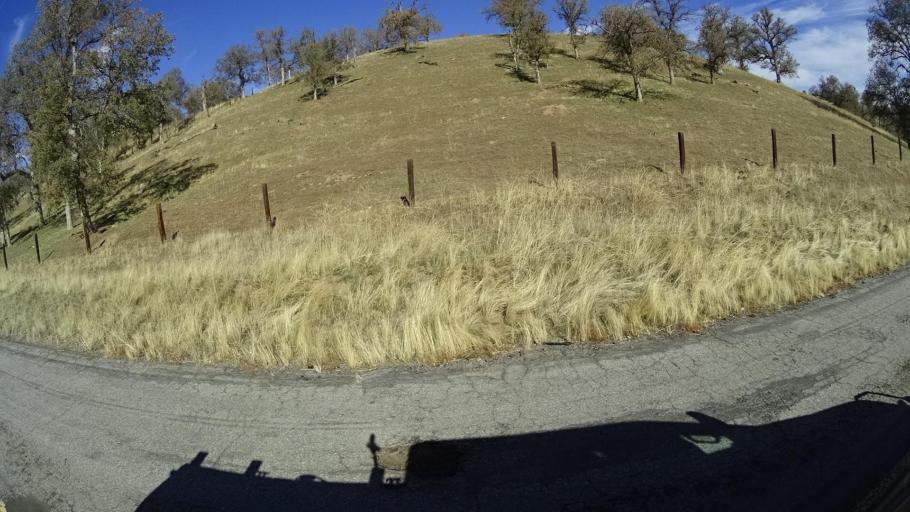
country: US
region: California
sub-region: Kern County
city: Alta Sierra
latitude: 35.6311
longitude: -118.7736
